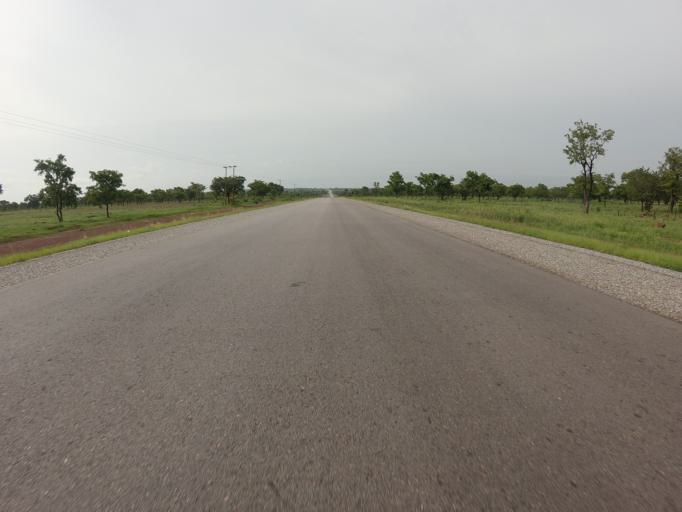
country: GH
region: Northern
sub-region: Yendi
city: Yendi
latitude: 9.6356
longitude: -0.0619
